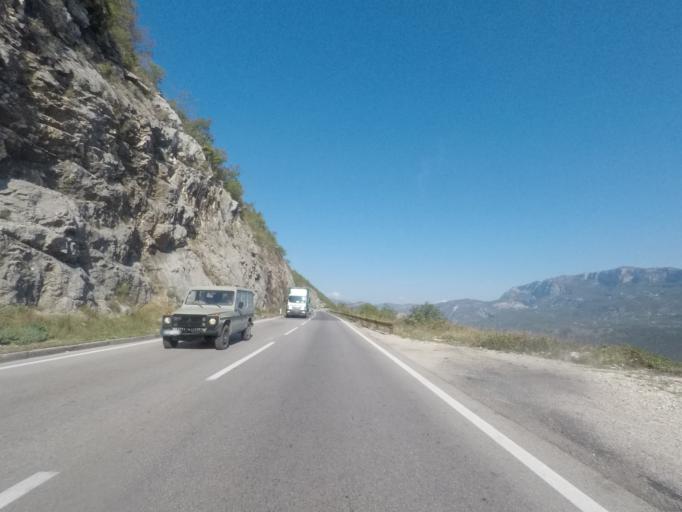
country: ME
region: Danilovgrad
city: Danilovgrad
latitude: 42.6197
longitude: 19.0196
